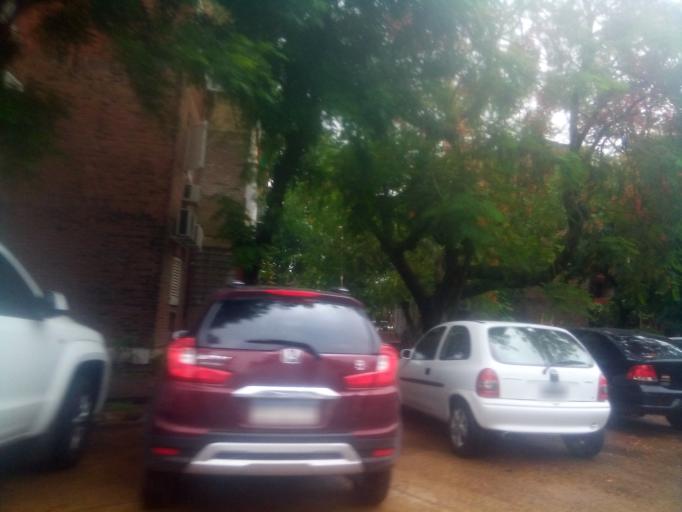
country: AR
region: Corrientes
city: Corrientes
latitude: -27.4627
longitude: -58.8287
